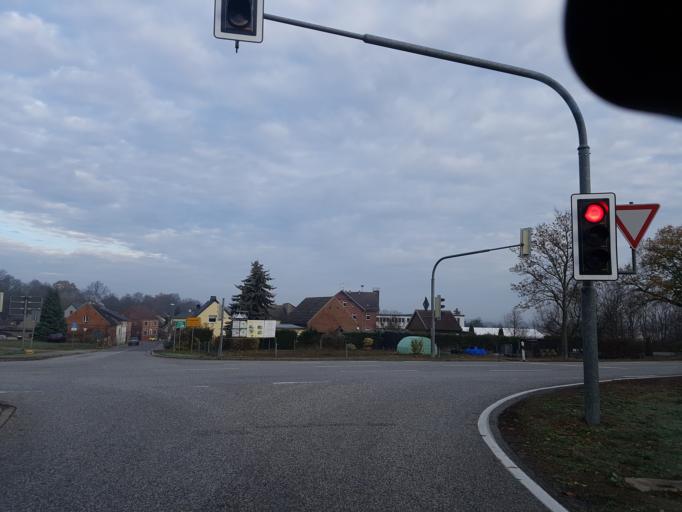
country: DE
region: Saxony-Anhalt
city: Kropstadt
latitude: 51.9595
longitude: 12.7466
